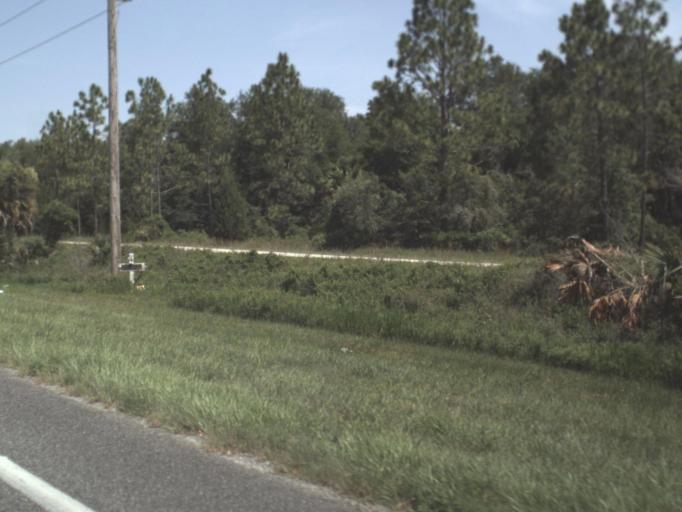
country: US
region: Florida
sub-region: Dixie County
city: Cross City
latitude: 29.6220
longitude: -83.1039
